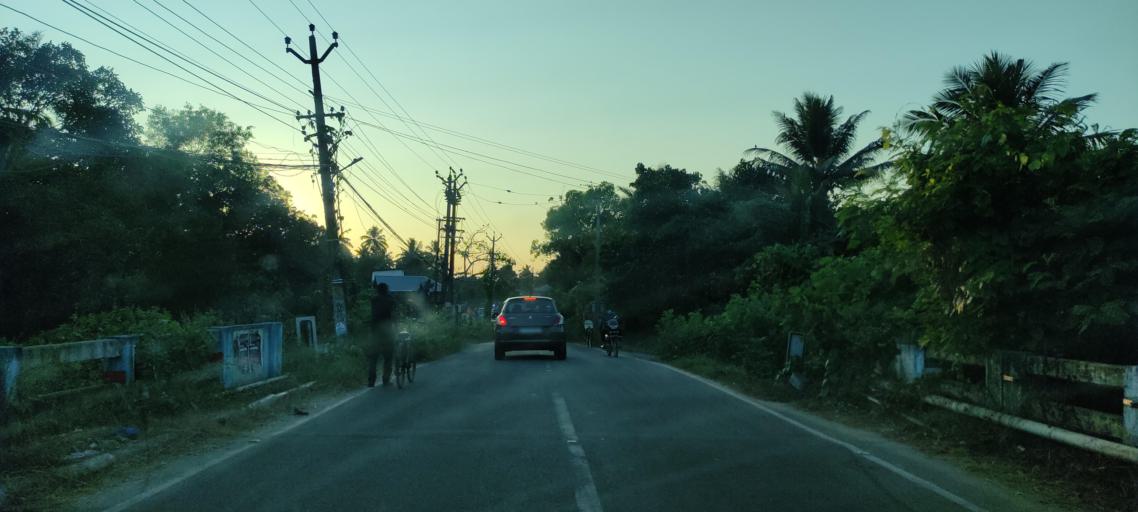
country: IN
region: Kerala
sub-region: Alappuzha
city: Kayankulam
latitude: 9.2601
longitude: 76.4471
